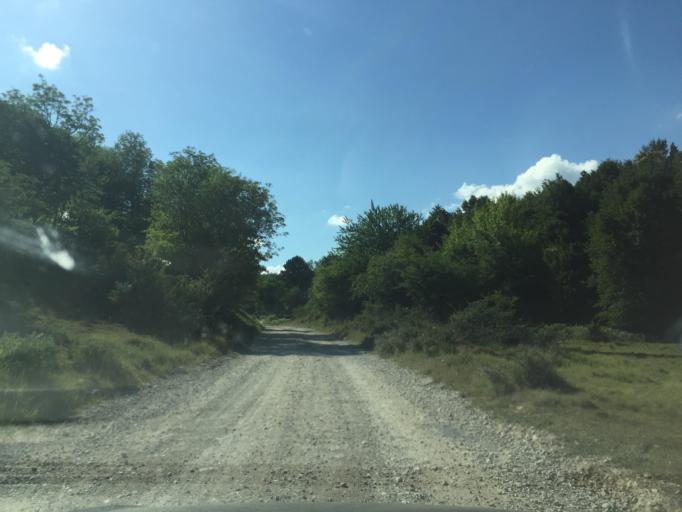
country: HR
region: Primorsko-Goranska
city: Klana
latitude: 45.4685
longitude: 14.4065
